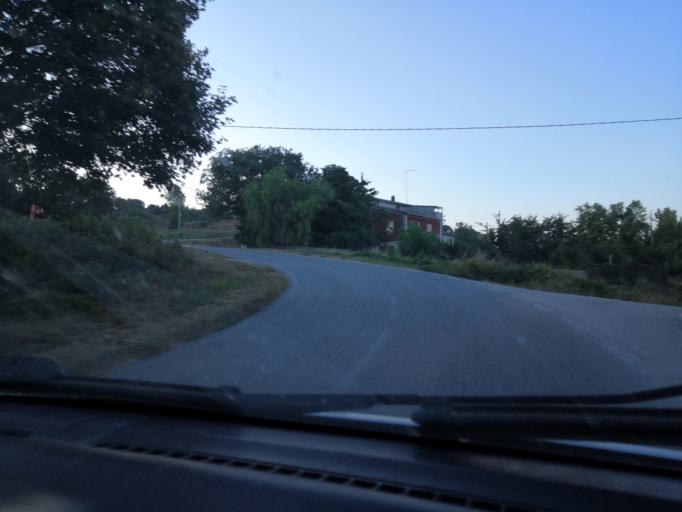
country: IT
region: Molise
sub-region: Provincia di Campobasso
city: Jelsi
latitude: 41.5144
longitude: 14.7848
